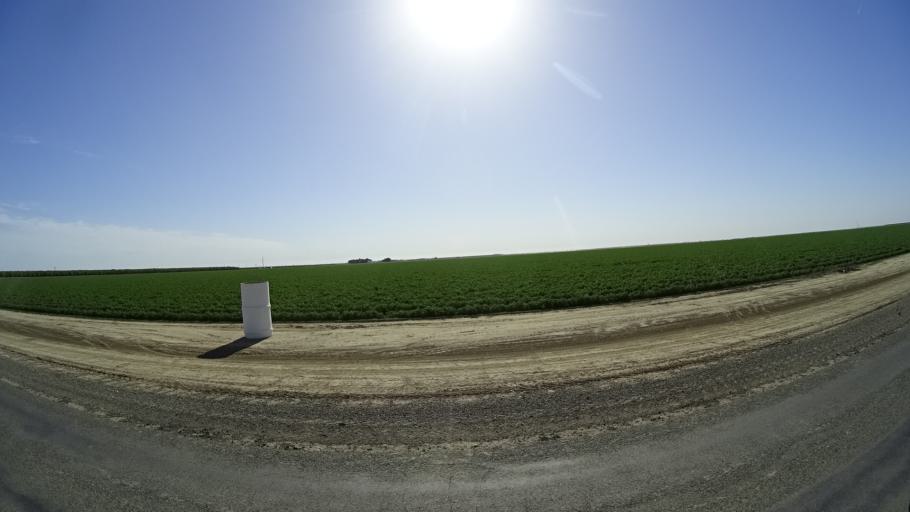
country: US
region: California
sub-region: Fresno County
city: Huron
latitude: 36.1344
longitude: -120.0038
